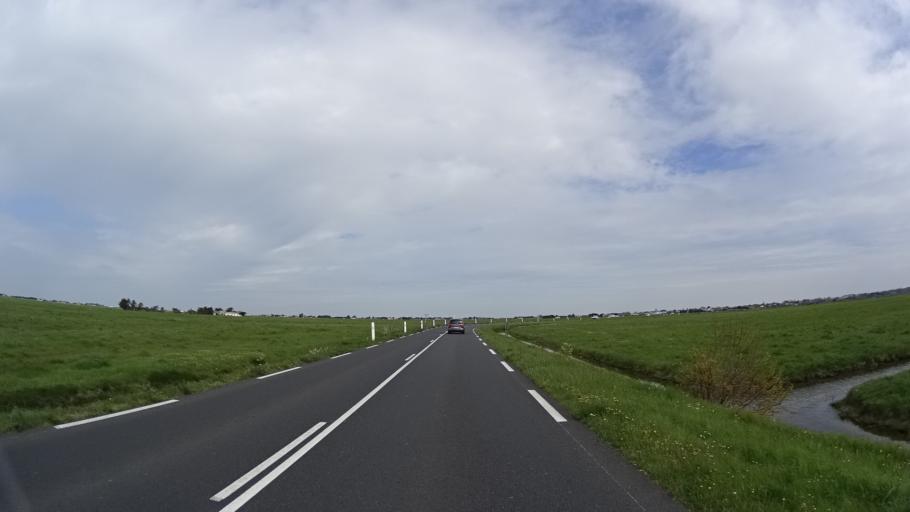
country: FR
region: Pays de la Loire
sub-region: Departement de la Vendee
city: Beauvoir-sur-Mer
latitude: 46.8986
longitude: -2.0633
